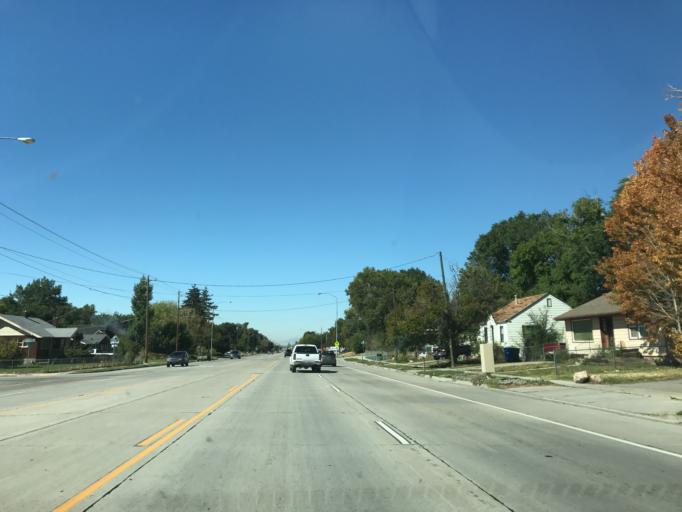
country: US
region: Utah
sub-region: Weber County
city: Ogden
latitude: 41.2442
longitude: -111.9588
